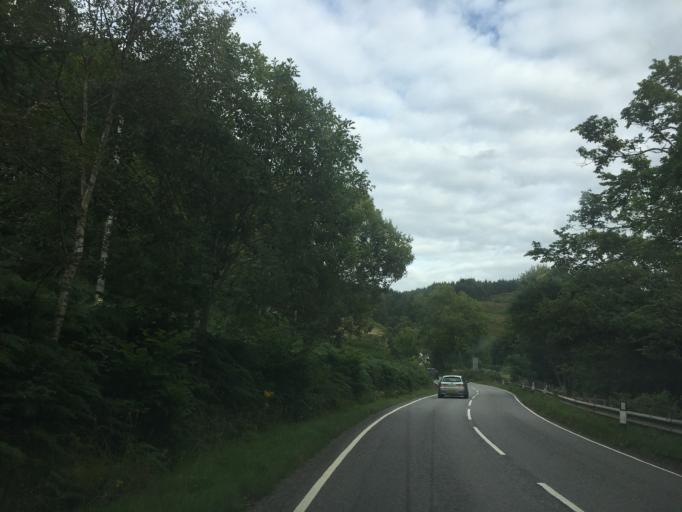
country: GB
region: Scotland
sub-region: Argyll and Bute
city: Oban
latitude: 56.3302
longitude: -5.5079
